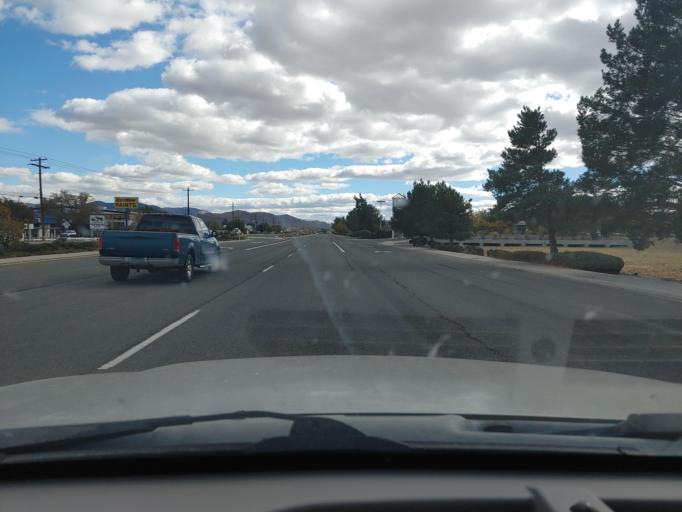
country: US
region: Nevada
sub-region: Carson City
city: Carson City
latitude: 39.1895
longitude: -119.7726
